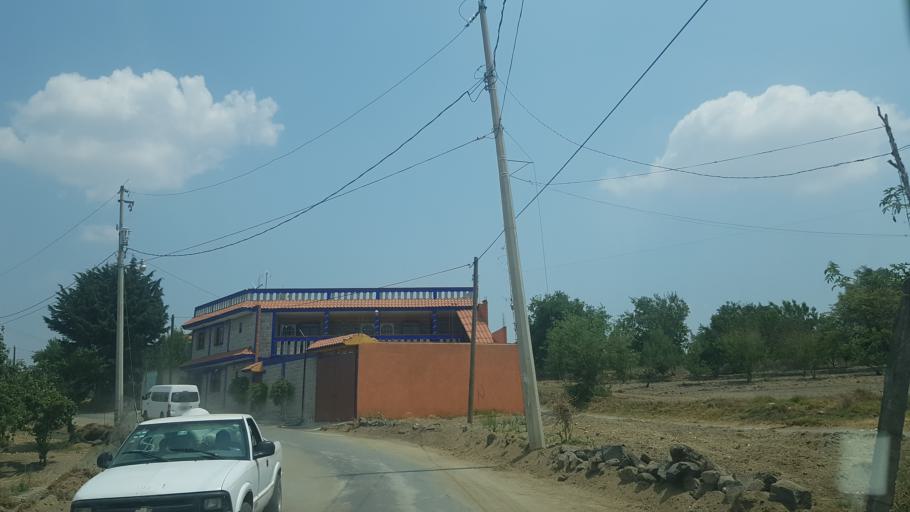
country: MX
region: Puebla
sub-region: San Nicolas de los Ranchos
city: San Pedro Yancuitlalpan
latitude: 19.0812
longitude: -98.4800
